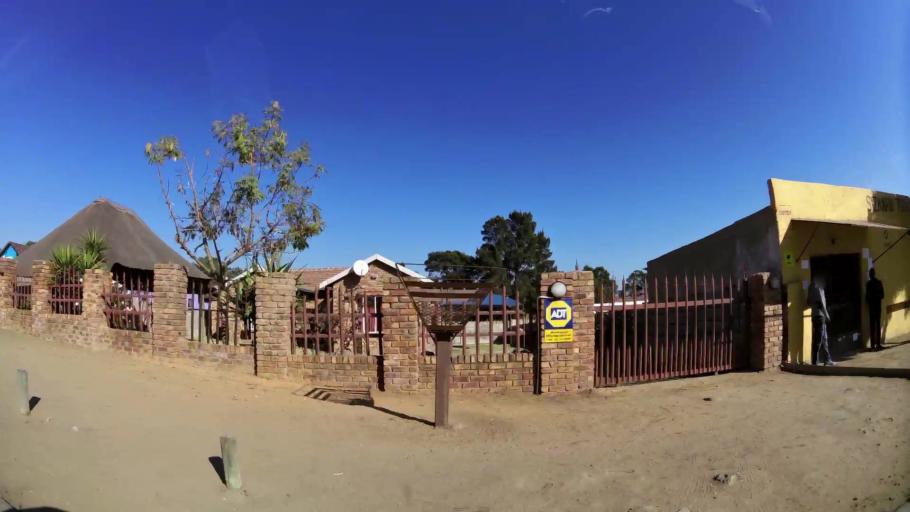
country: ZA
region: Gauteng
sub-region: City of Johannesburg Metropolitan Municipality
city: Modderfontein
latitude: -26.0477
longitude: 28.1955
